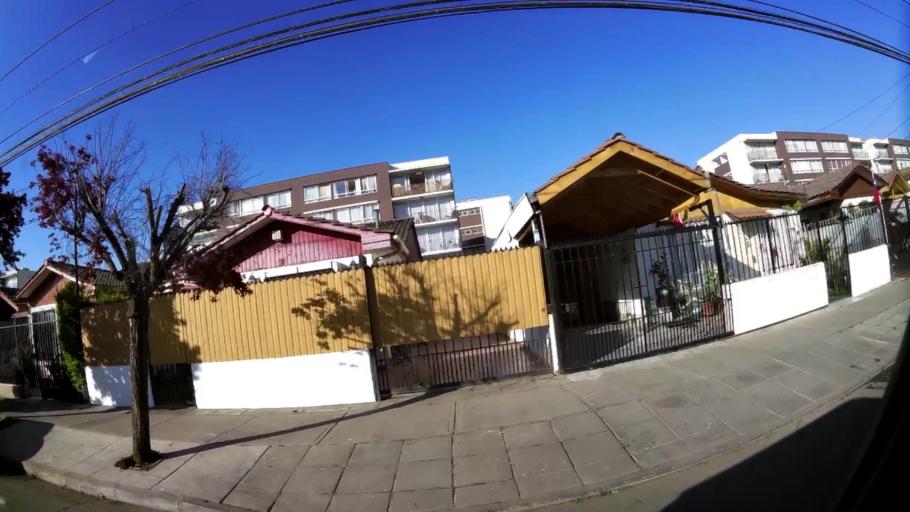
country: CL
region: Santiago Metropolitan
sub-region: Provincia de Santiago
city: Lo Prado
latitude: -33.4836
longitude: -70.7560
